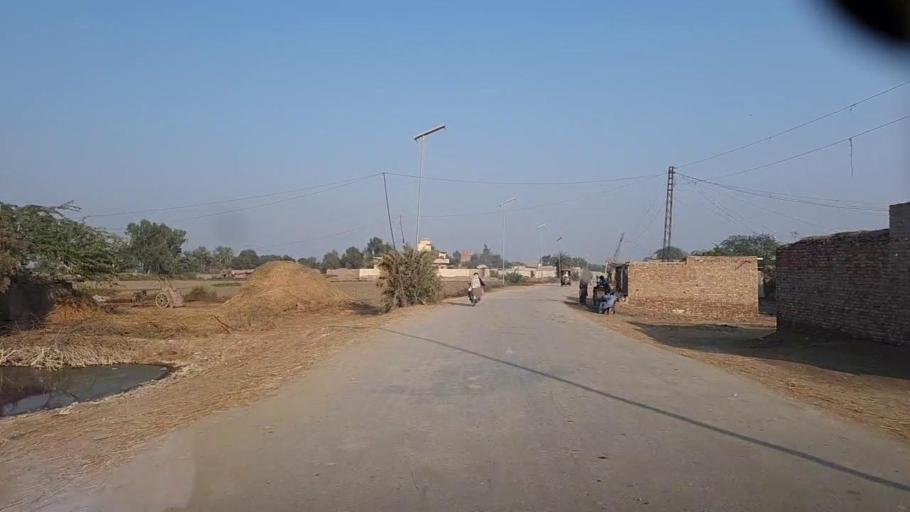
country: PK
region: Sindh
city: Jacobabad
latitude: 28.2387
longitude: 68.4765
